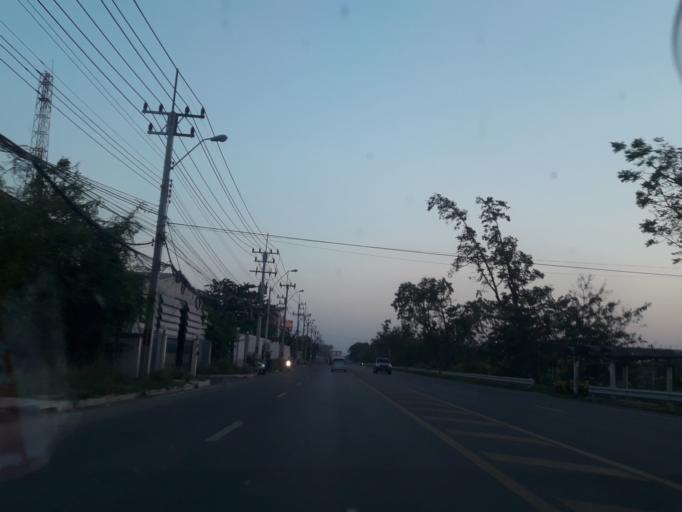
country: TH
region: Pathum Thani
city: Khlong Luang
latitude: 14.0884
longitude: 100.7103
